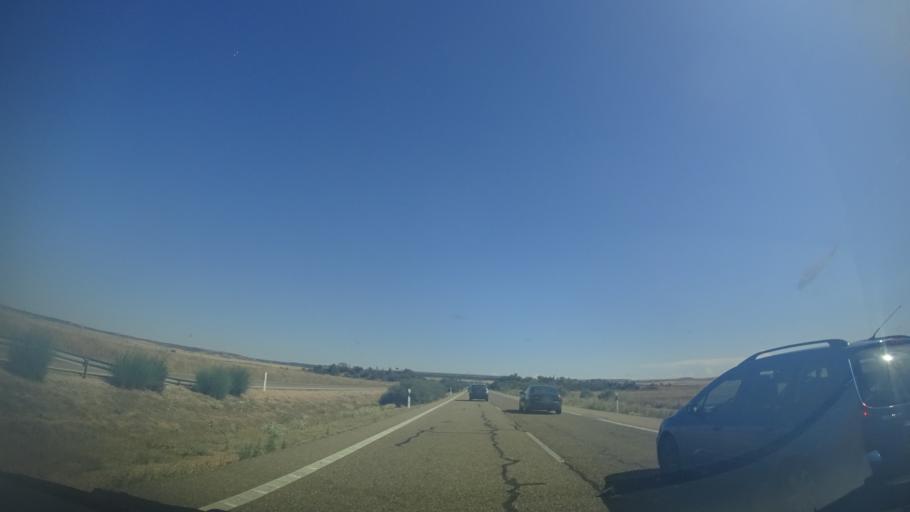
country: ES
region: Castille and Leon
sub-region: Provincia de Valladolid
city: Villanueva de los Caballeros
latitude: 41.7510
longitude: -5.2819
